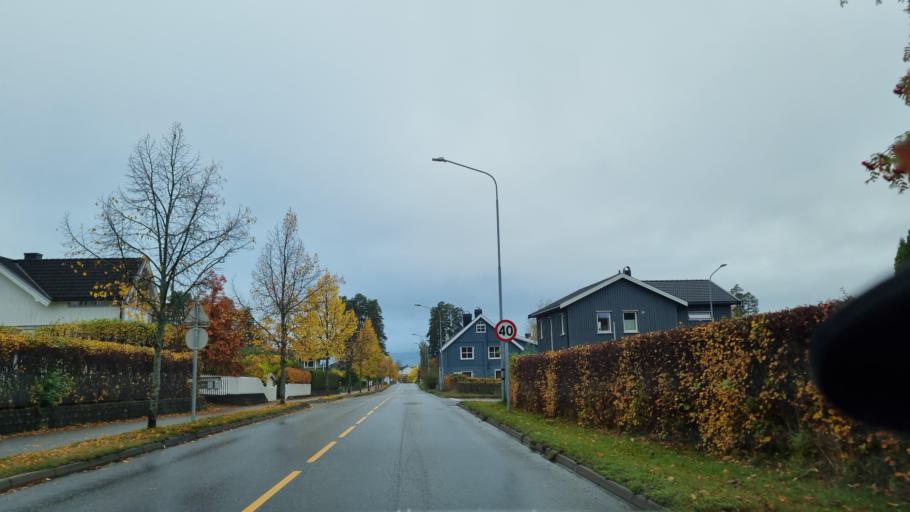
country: NO
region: Hedmark
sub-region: Hamar
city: Hamar
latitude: 60.8015
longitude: 11.0624
